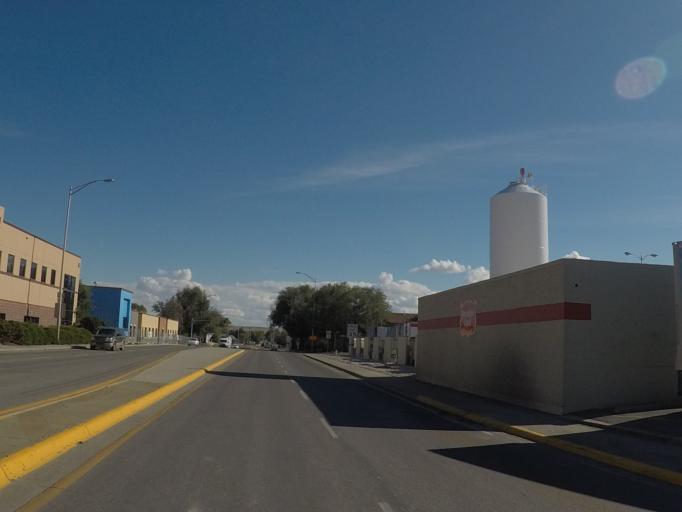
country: US
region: Montana
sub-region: Yellowstone County
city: Billings
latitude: 45.7800
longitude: -108.5020
